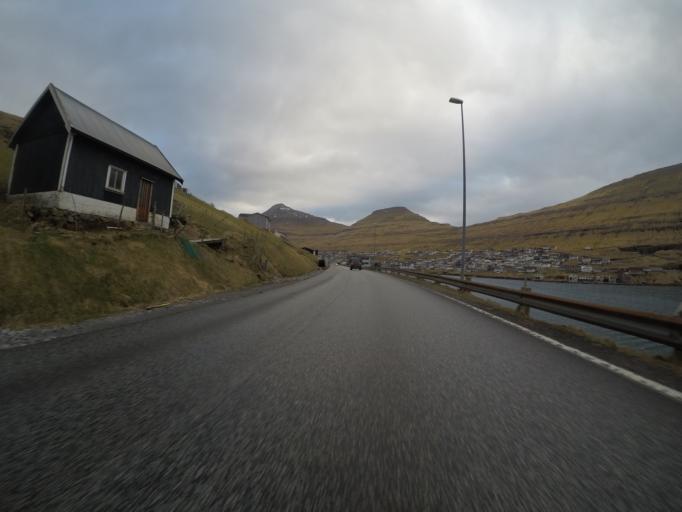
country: FO
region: Nordoyar
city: Klaksvik
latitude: 62.2407
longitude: -6.5923
